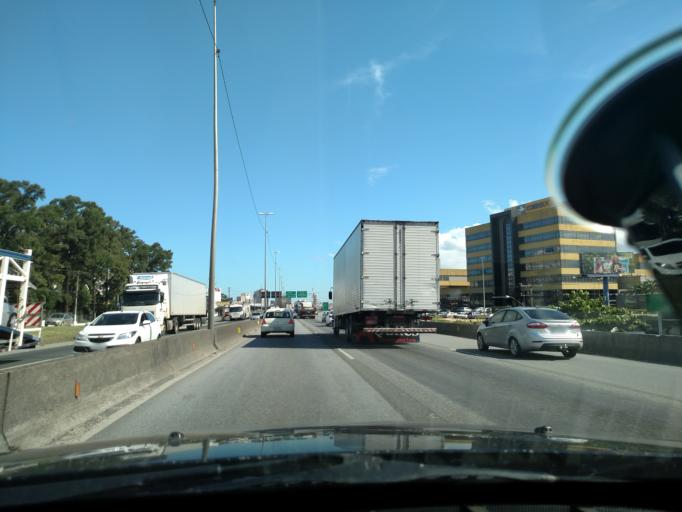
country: BR
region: Santa Catarina
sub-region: Sao Jose
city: Campinas
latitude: -27.5741
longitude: -48.6136
